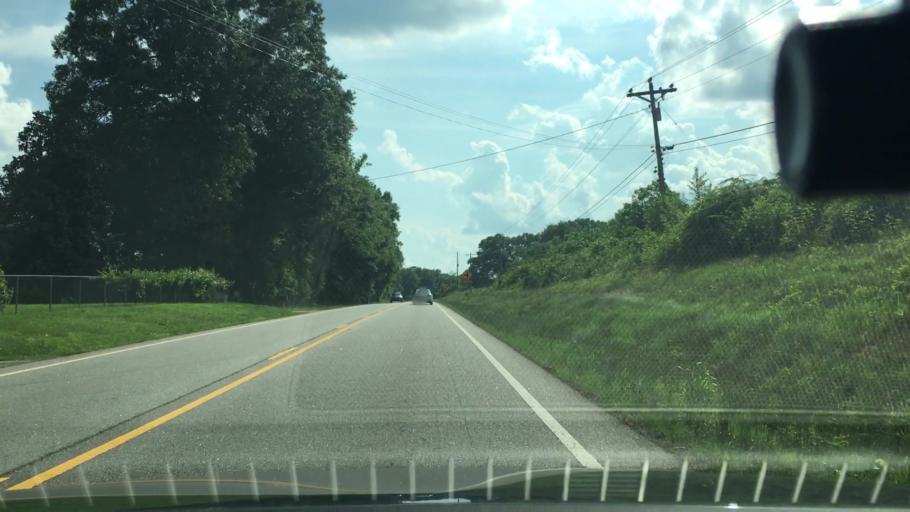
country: US
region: Georgia
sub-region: Spalding County
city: Experiment
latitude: 33.2397
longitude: -84.3996
